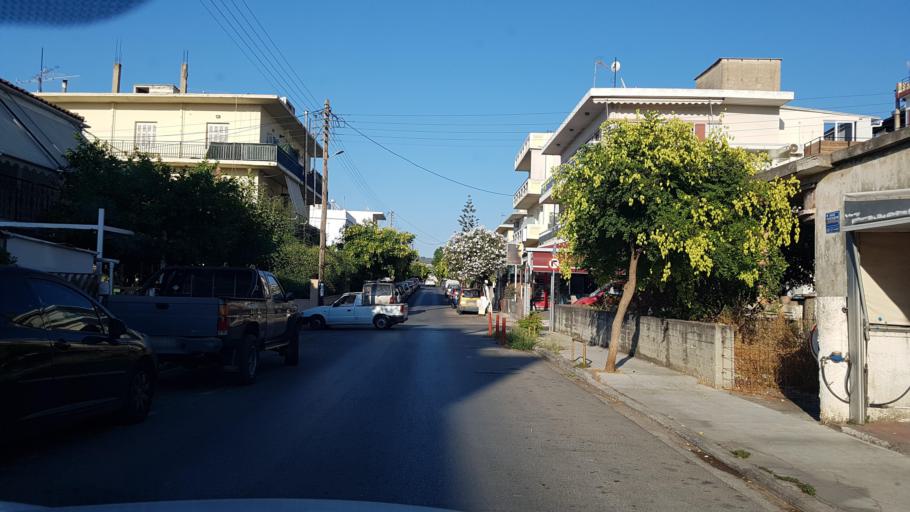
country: GR
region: Crete
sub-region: Nomos Chanias
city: Chania
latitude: 35.5074
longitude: 24.0137
